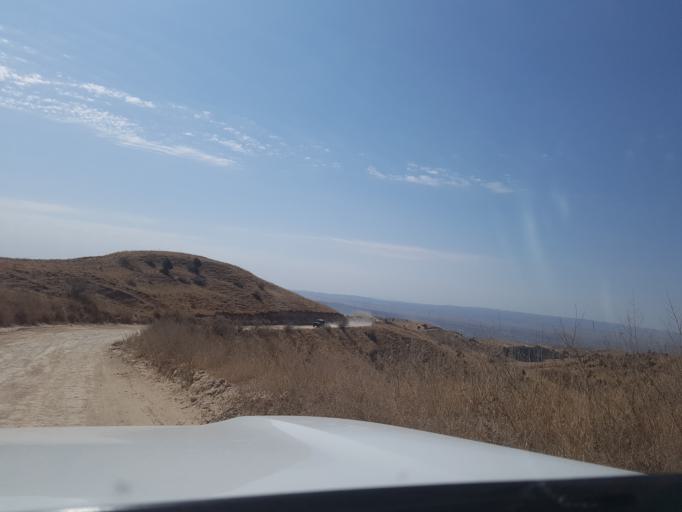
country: TM
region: Ahal
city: Baharly
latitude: 38.2940
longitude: 56.9353
